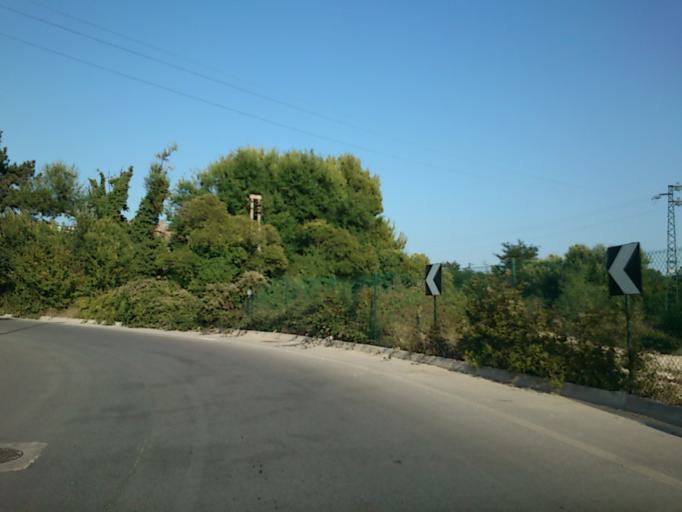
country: IT
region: The Marches
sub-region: Provincia di Pesaro e Urbino
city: Fano
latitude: 43.8263
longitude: 13.0448
